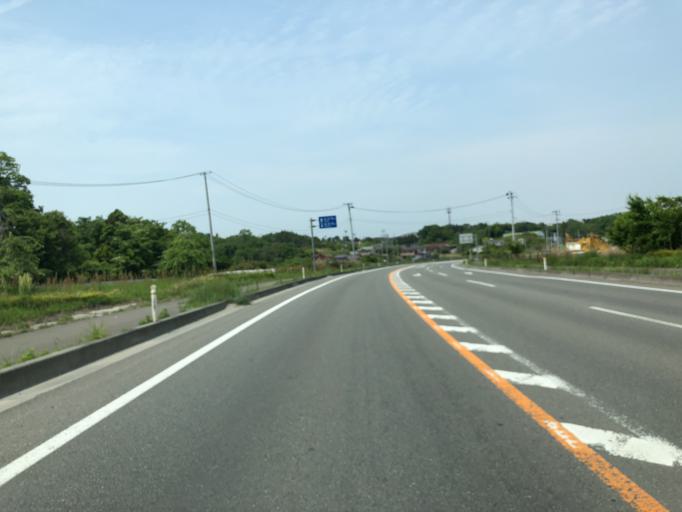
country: JP
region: Miyagi
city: Marumori
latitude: 37.8552
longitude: 140.9203
